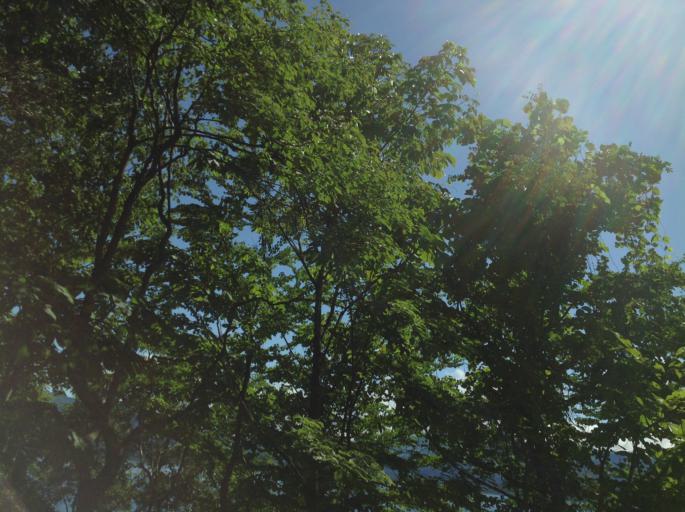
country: JP
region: Akita
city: Kakunodatemachi
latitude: 39.7092
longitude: 140.6375
